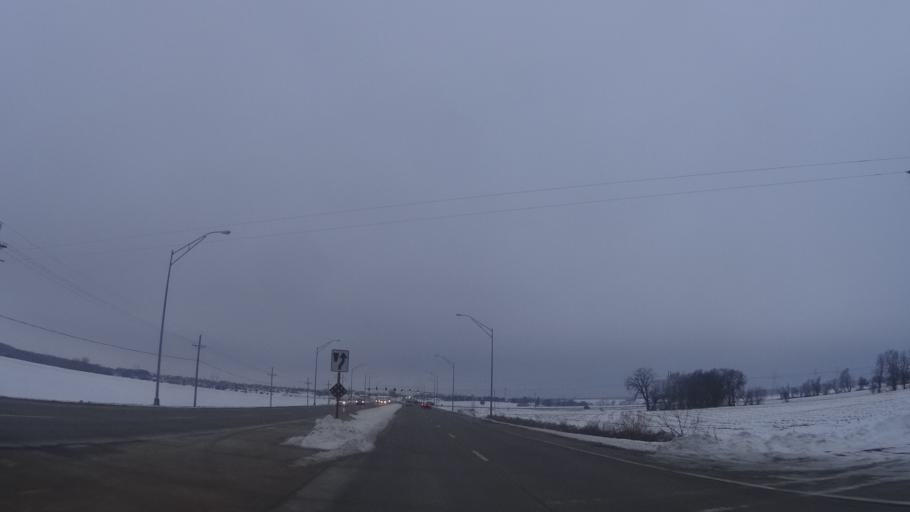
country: US
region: Nebraska
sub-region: Sarpy County
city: La Vista
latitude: 41.1618
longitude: -95.9811
